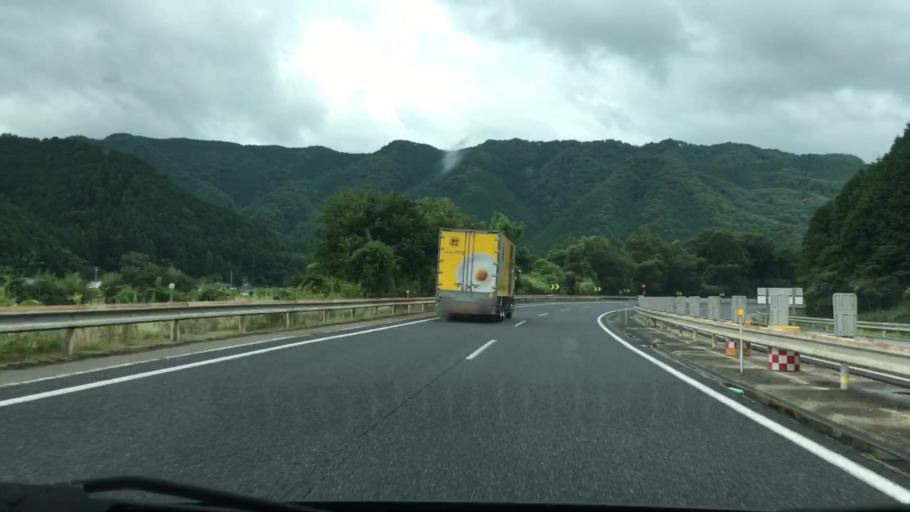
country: JP
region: Okayama
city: Takahashi
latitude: 34.9866
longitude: 133.7132
